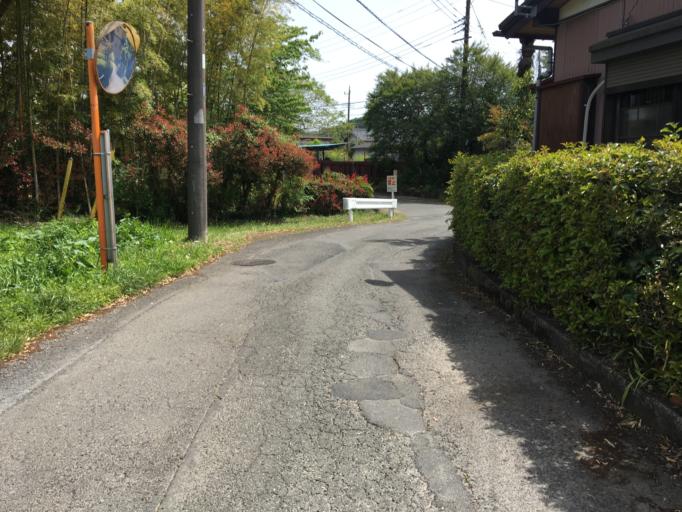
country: JP
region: Saitama
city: Hanno
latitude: 35.8896
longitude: 139.3199
